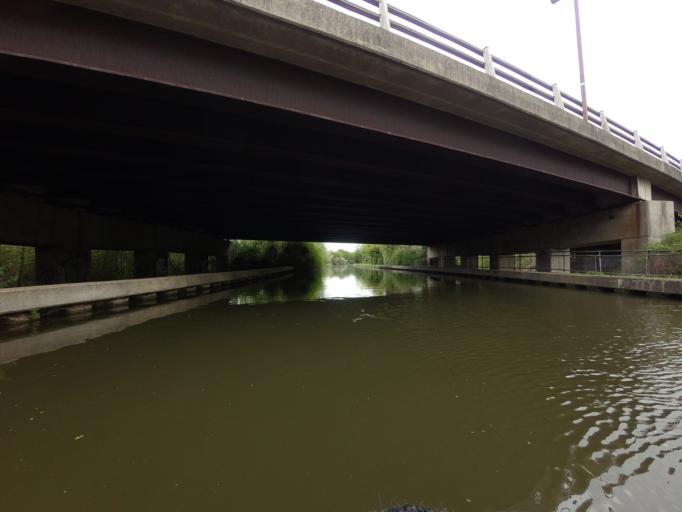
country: GB
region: England
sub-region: Milton Keynes
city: Water Eaton
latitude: 52.0060
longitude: -0.7169
